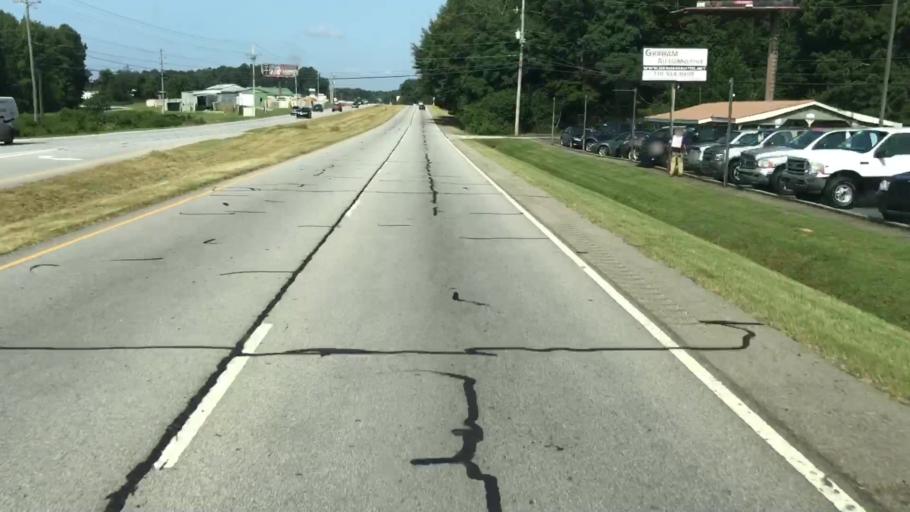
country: US
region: Georgia
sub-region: Walton County
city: Loganville
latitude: 33.8297
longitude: -83.8453
